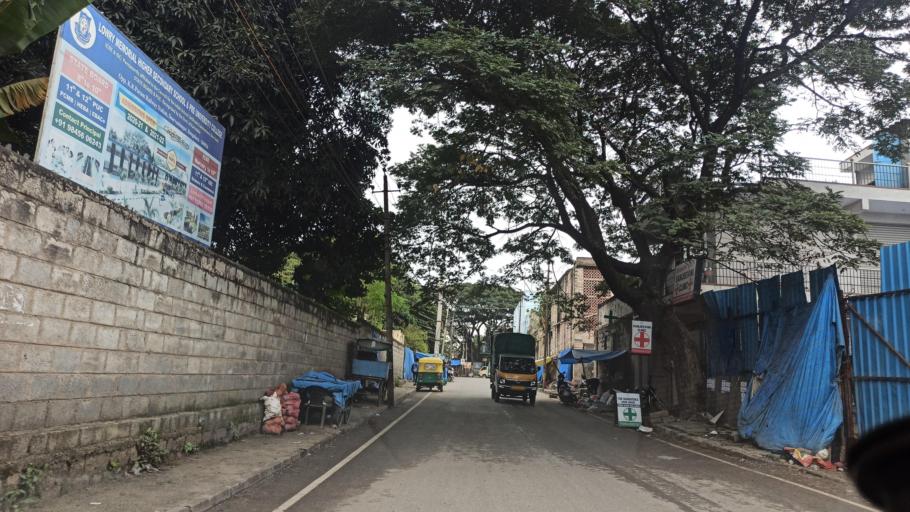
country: IN
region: Karnataka
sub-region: Bangalore Urban
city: Bangalore
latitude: 12.9994
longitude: 77.6767
